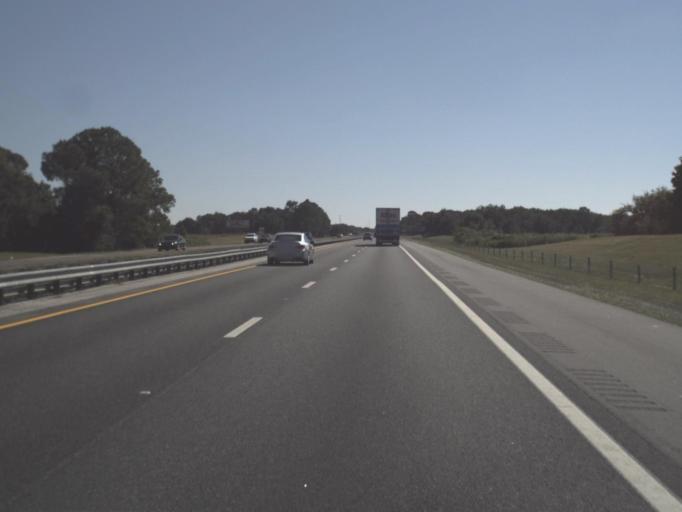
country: US
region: Florida
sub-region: Lake County
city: Hawthorne
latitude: 28.6963
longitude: -81.8766
